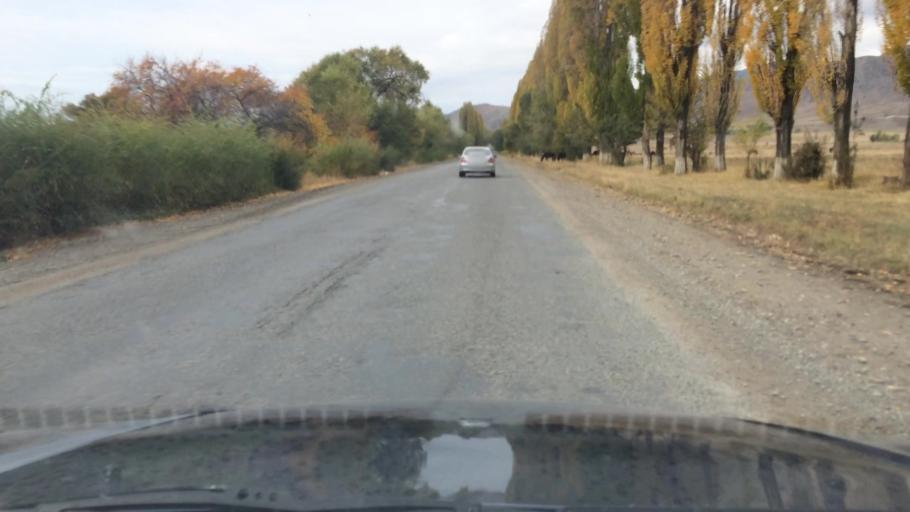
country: KG
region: Ysyk-Koel
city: Pokrovka
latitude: 42.7378
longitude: 77.9244
